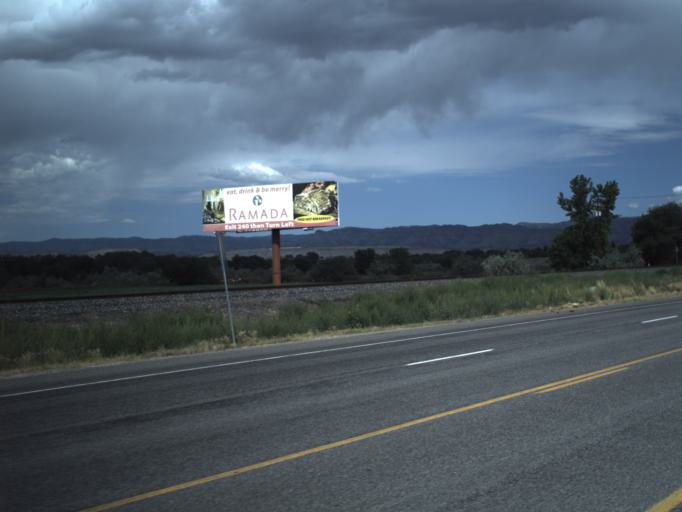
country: US
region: Utah
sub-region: Carbon County
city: Price
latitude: 39.5798
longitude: -110.7864
